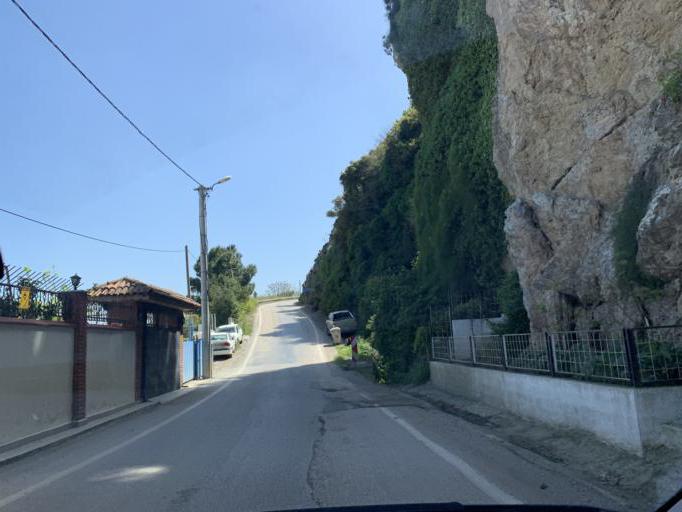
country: TR
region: Bursa
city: Niluefer
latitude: 40.3555
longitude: 28.9735
